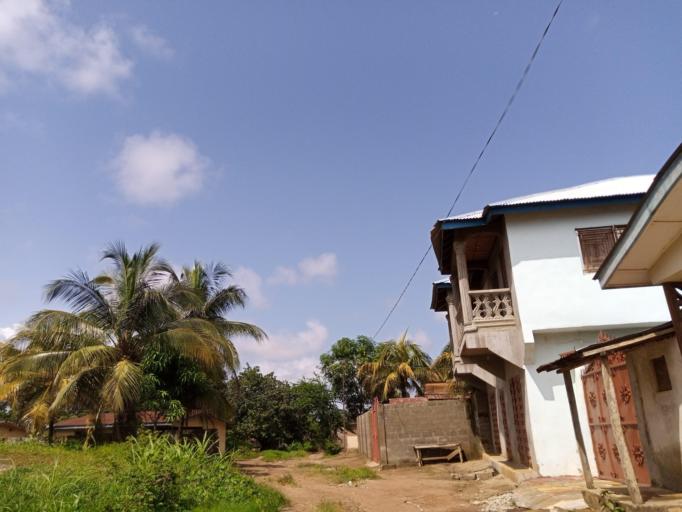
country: SL
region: Northern Province
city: Tintafor
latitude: 8.6255
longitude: -13.2117
